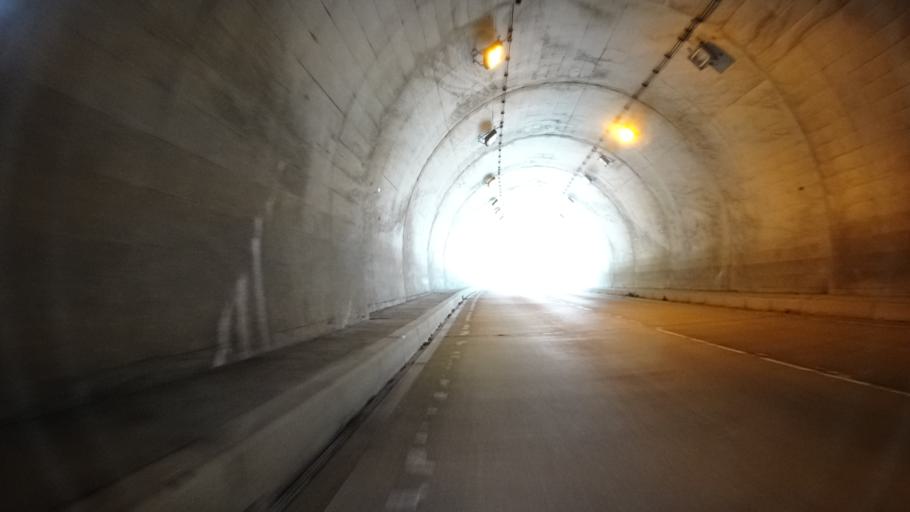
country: JP
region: Yamanashi
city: Nirasaki
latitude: 35.8684
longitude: 138.5052
